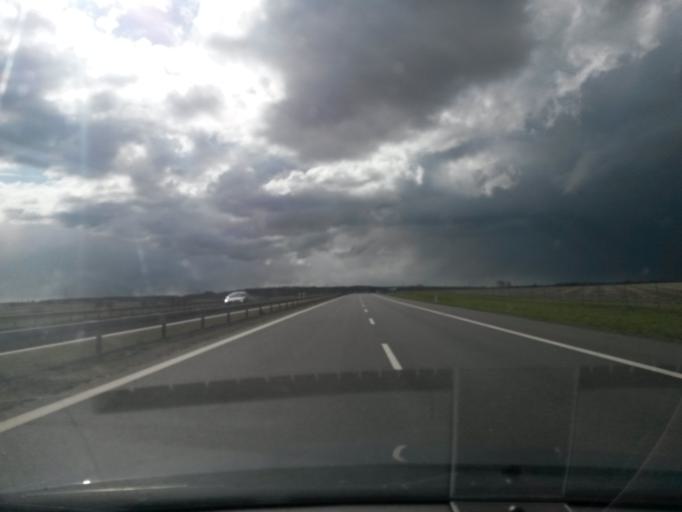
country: PL
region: Greater Poland Voivodeship
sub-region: Powiat sredzki
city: Dominowo
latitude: 52.3131
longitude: 17.3891
